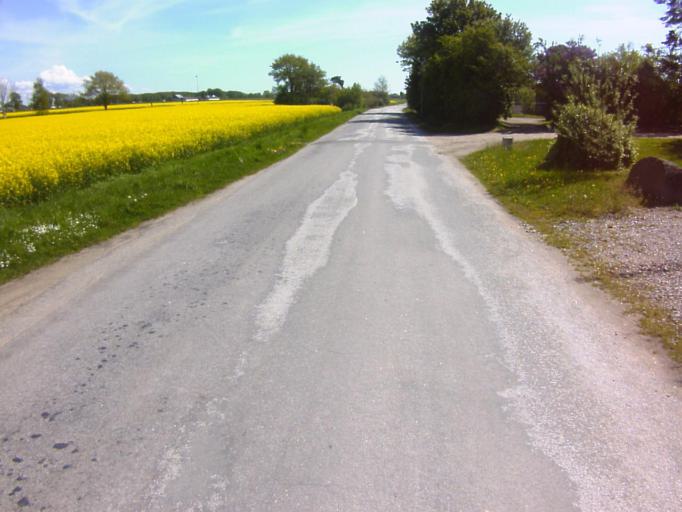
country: SE
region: Blekinge
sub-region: Solvesborgs Kommun
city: Soelvesborg
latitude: 56.0548
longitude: 14.6349
